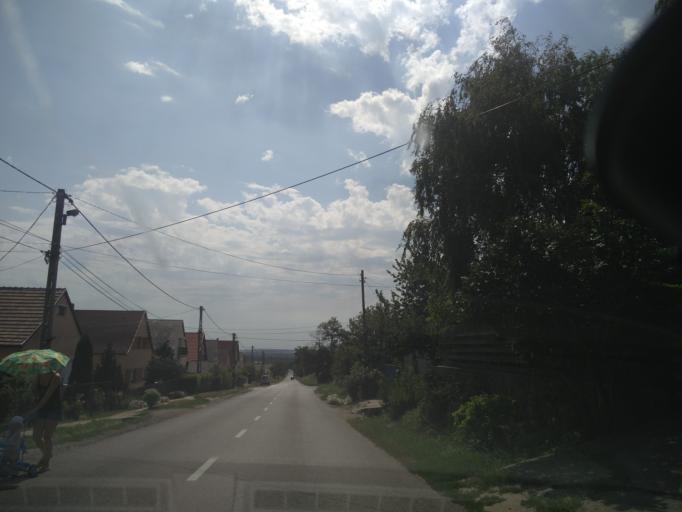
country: HU
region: Fejer
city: Velence
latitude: 47.2577
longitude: 18.6207
